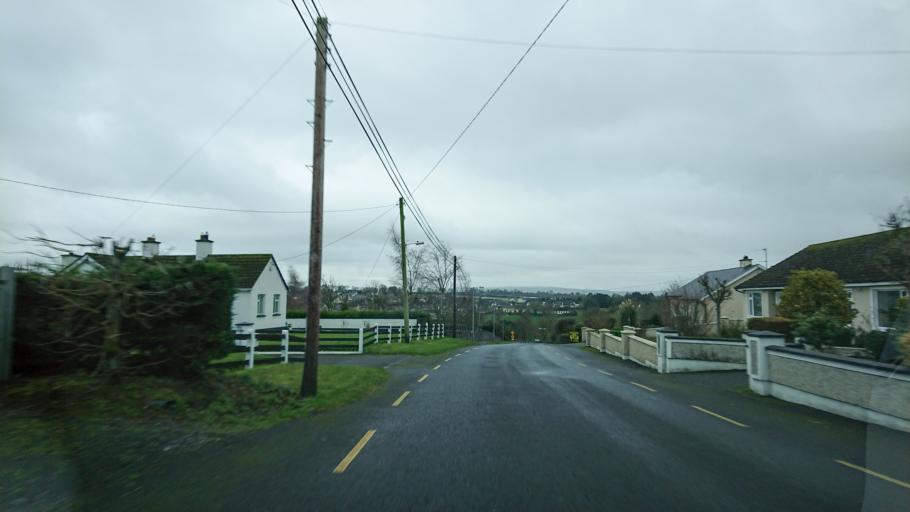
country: IE
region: Leinster
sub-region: Kilkenny
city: Kilkenny
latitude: 52.5450
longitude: -7.2724
